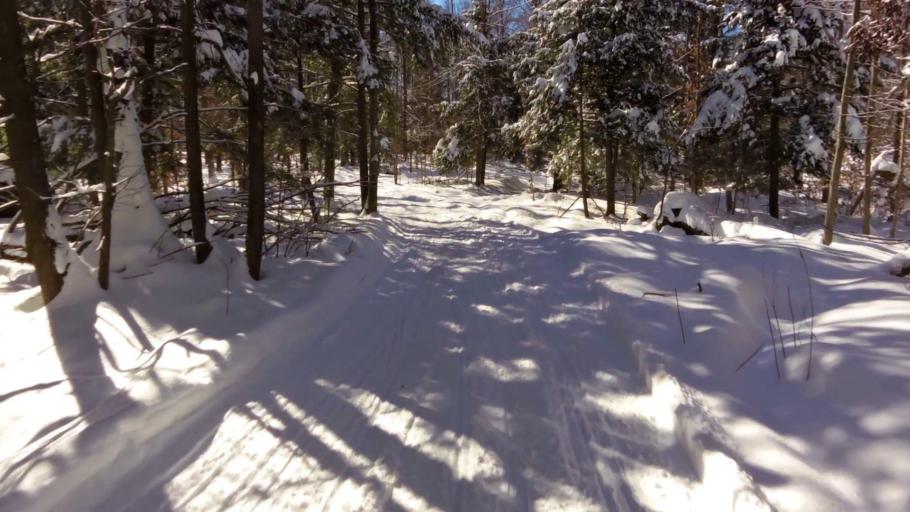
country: US
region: New York
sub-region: Chautauqua County
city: Mayville
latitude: 42.2316
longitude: -79.5217
